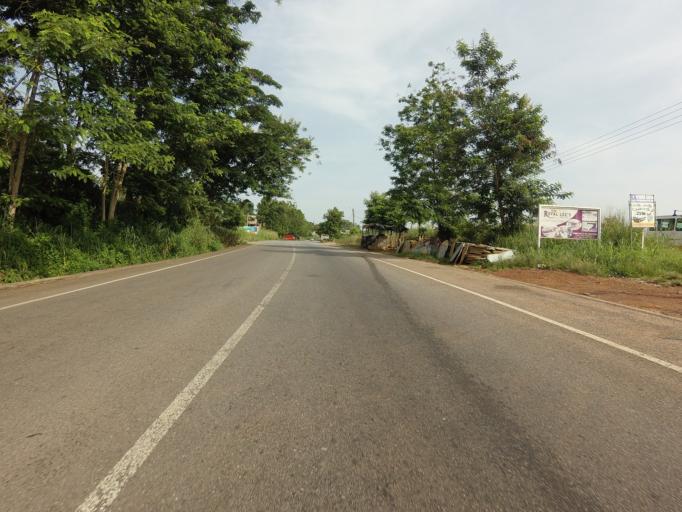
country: GH
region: Eastern
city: Aburi
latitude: 5.8830
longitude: -0.1552
